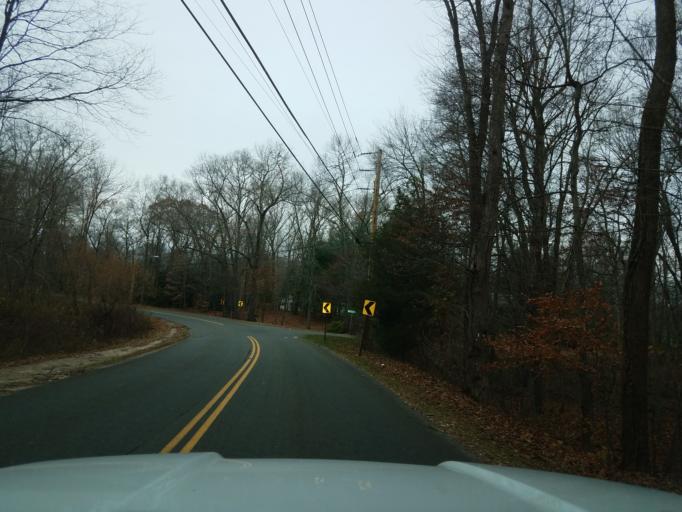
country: US
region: Connecticut
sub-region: New Haven County
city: Guilford
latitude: 41.3264
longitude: -72.7145
